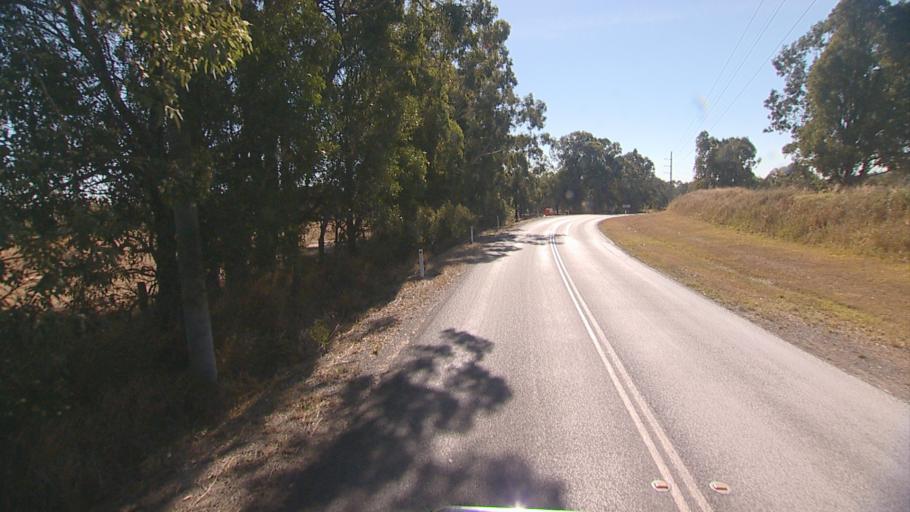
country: AU
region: Queensland
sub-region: Logan
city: Cedar Vale
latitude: -27.8622
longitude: 153.0180
